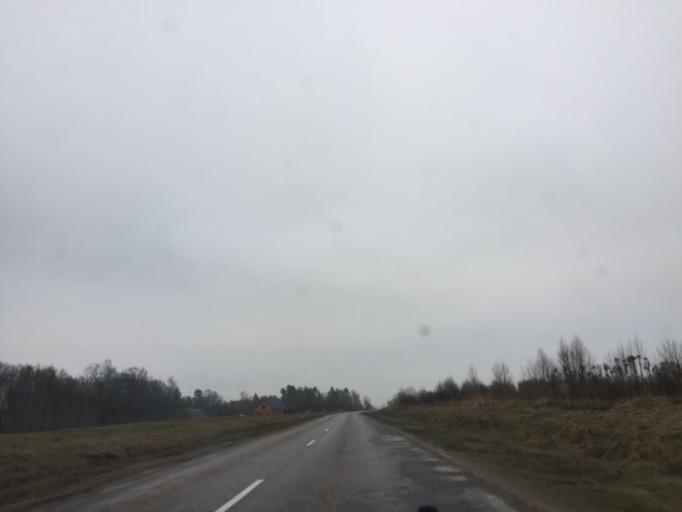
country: LV
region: Limbazu Rajons
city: Limbazi
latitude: 57.5336
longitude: 24.6877
